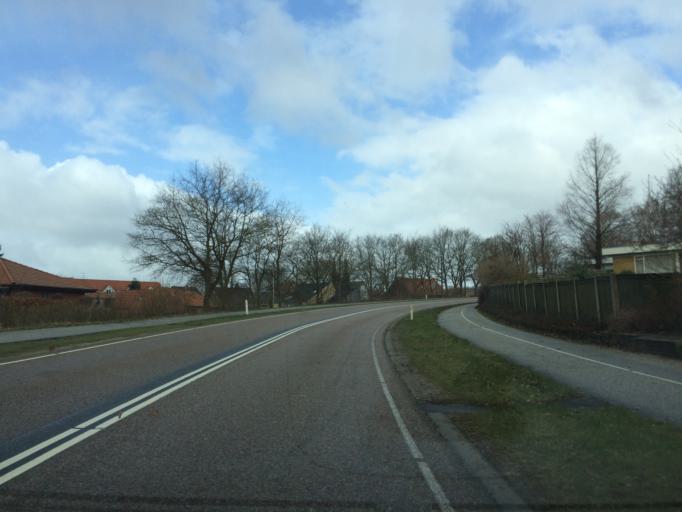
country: DK
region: Central Jutland
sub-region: Silkeborg Kommune
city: Silkeborg
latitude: 56.1555
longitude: 9.5343
